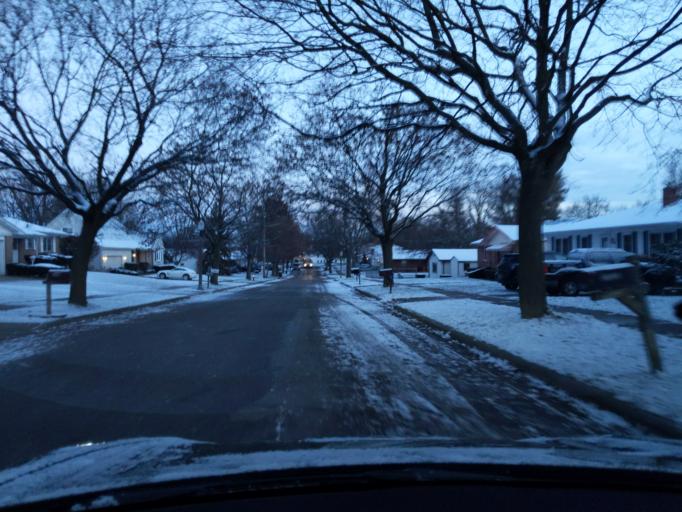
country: US
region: Michigan
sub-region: Ingham County
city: Lansing
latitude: 42.6922
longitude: -84.5643
